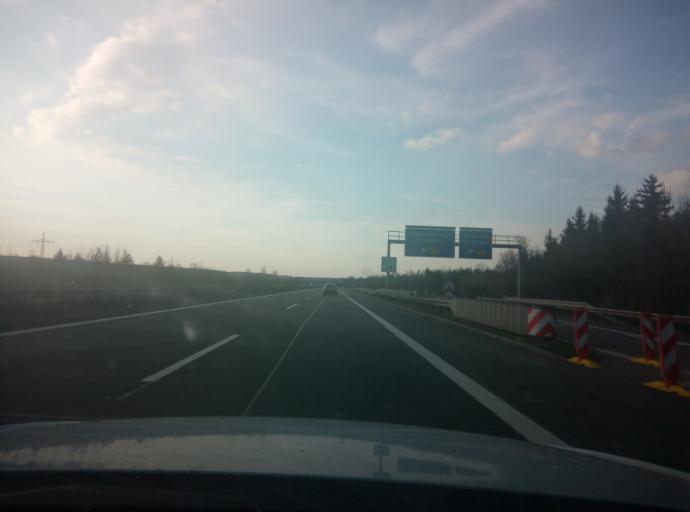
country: DE
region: Baden-Wuerttemberg
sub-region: Freiburg Region
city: Deisslingen
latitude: 48.0878
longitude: 8.5936
